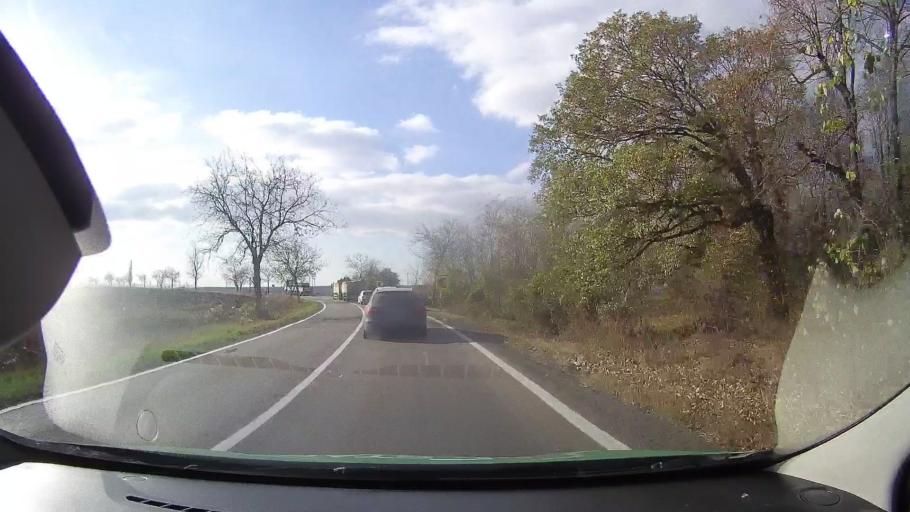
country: RO
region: Tulcea
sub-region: Comuna Topolog
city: Topolog
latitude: 44.9074
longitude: 28.4080
